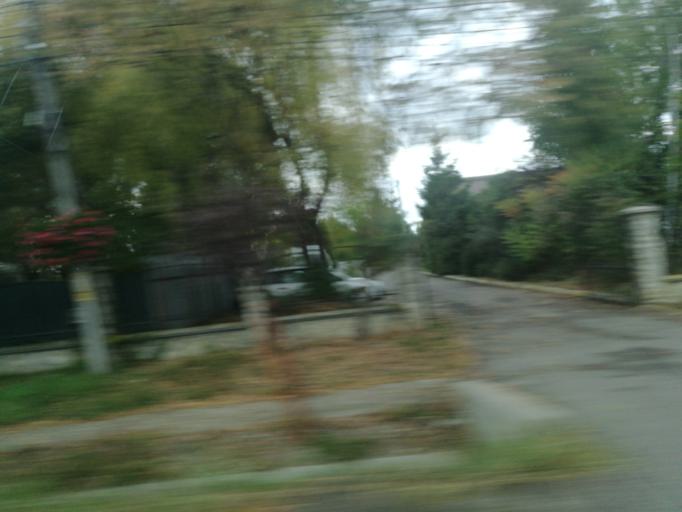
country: RO
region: Mures
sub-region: Comuna Ernei
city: Ernei
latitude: 46.5883
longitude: 24.6184
